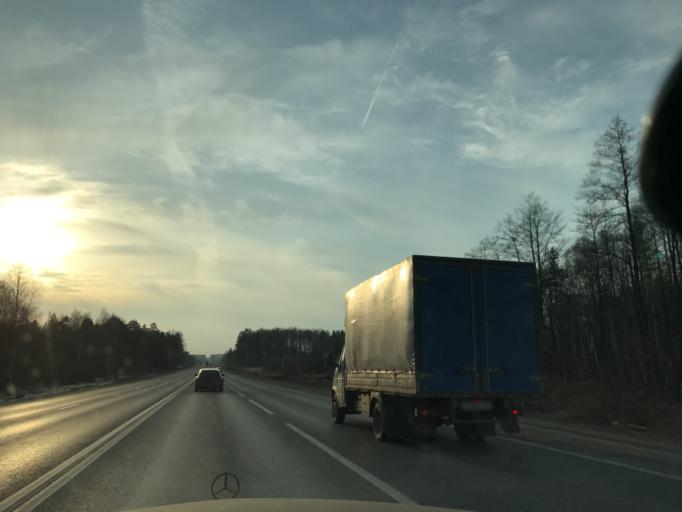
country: RU
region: Vladimir
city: Kosterevo
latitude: 55.9648
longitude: 39.7572
